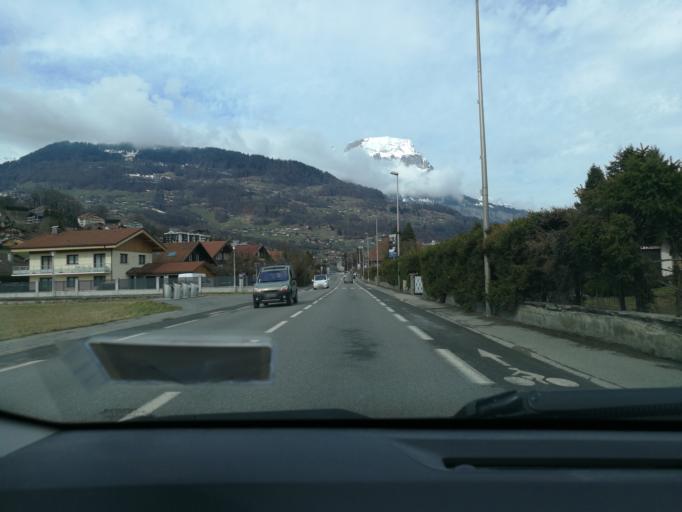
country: FR
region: Rhone-Alpes
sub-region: Departement de la Haute-Savoie
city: Sallanches
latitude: 45.9292
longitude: 6.6373
